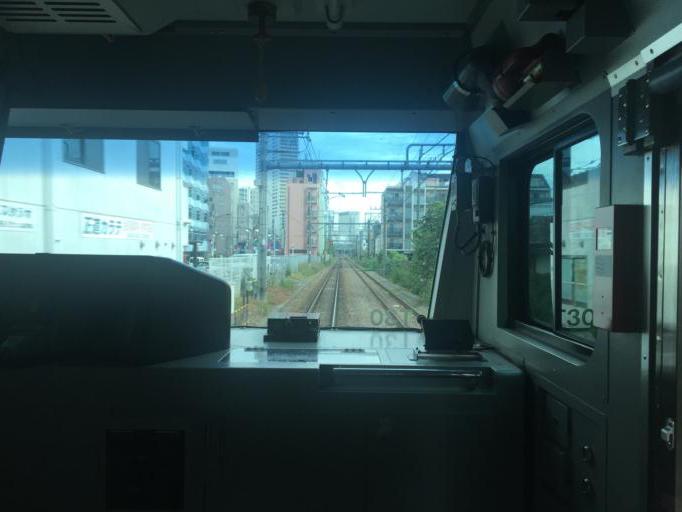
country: JP
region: Tokyo
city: Hino
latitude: 35.6997
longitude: 139.4062
